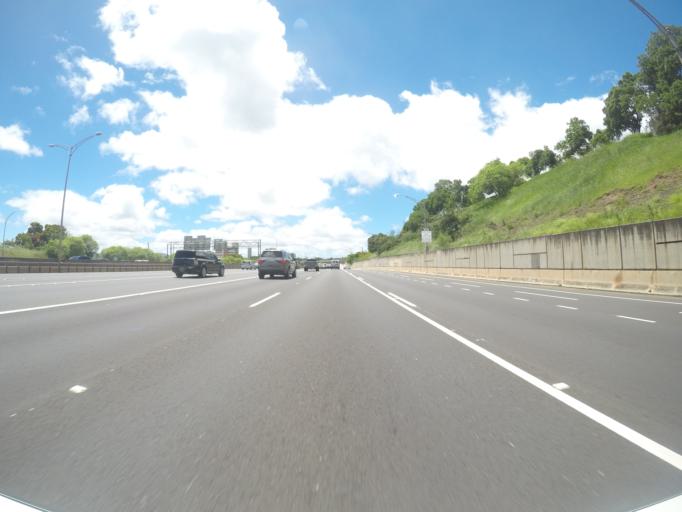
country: US
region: Hawaii
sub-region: Honolulu County
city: Halawa
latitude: 21.3776
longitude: -157.9272
